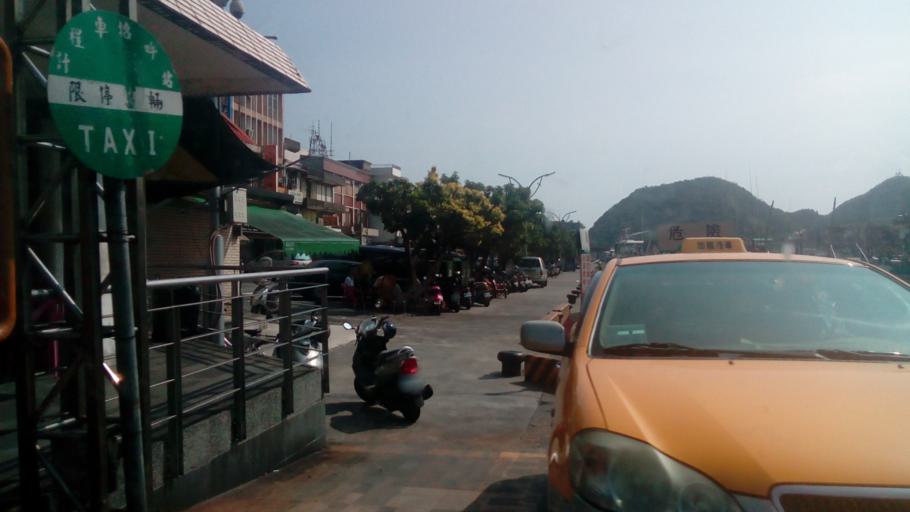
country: TW
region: Taiwan
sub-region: Yilan
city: Yilan
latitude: 24.5812
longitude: 121.8650
